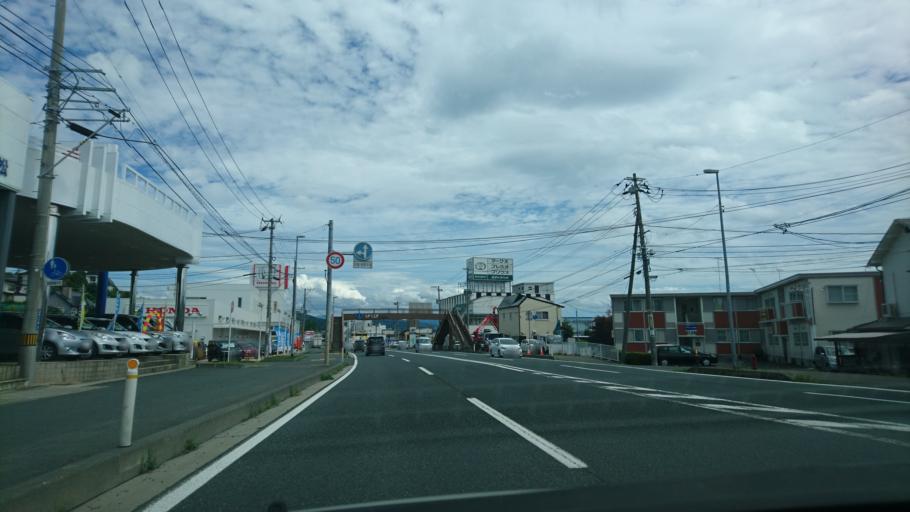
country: JP
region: Iwate
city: Morioka-shi
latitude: 39.7196
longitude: 141.1406
